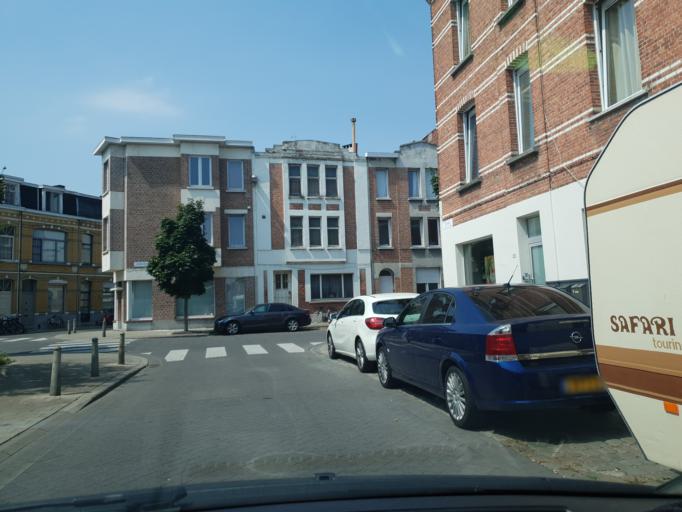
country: BE
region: Flanders
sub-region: Provincie Antwerpen
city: Borsbeek
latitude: 51.2222
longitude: 4.4665
